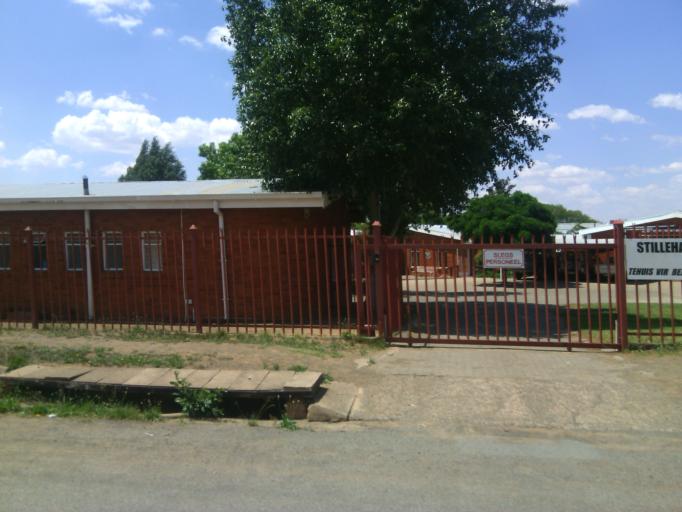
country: ZA
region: Orange Free State
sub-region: Xhariep District Municipality
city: Dewetsdorp
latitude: -29.5829
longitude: 26.6631
